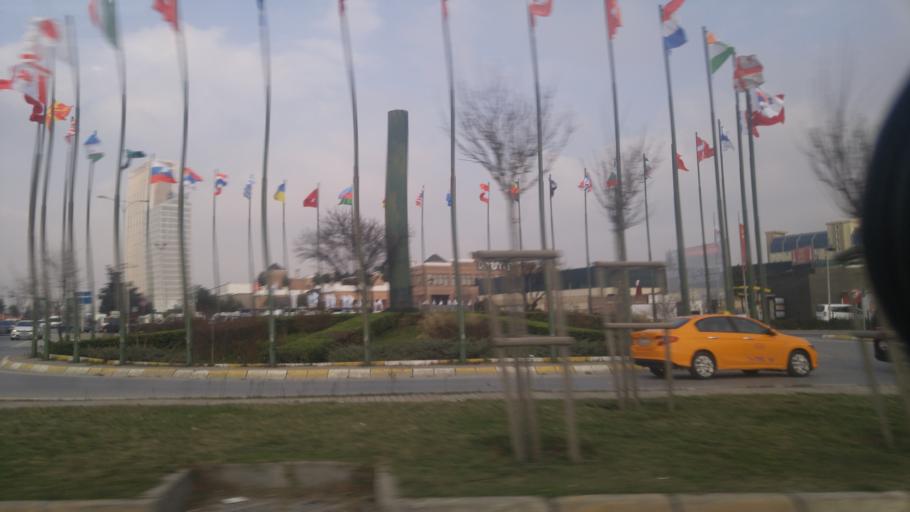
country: TR
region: Istanbul
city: Gurpinar
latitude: 41.0245
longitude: 28.6224
